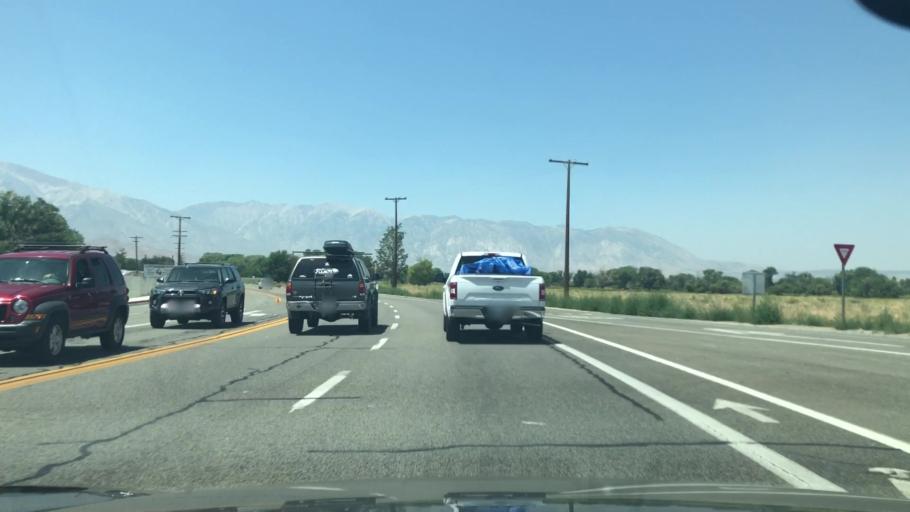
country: US
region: California
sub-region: Inyo County
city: Bishop
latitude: 37.3736
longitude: -118.3981
